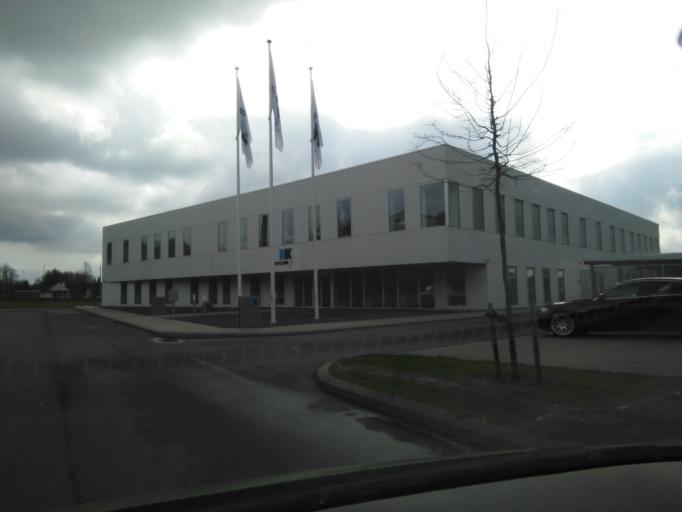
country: DK
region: Central Jutland
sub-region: Arhus Kommune
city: Stavtrup
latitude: 56.1542
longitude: 10.0957
